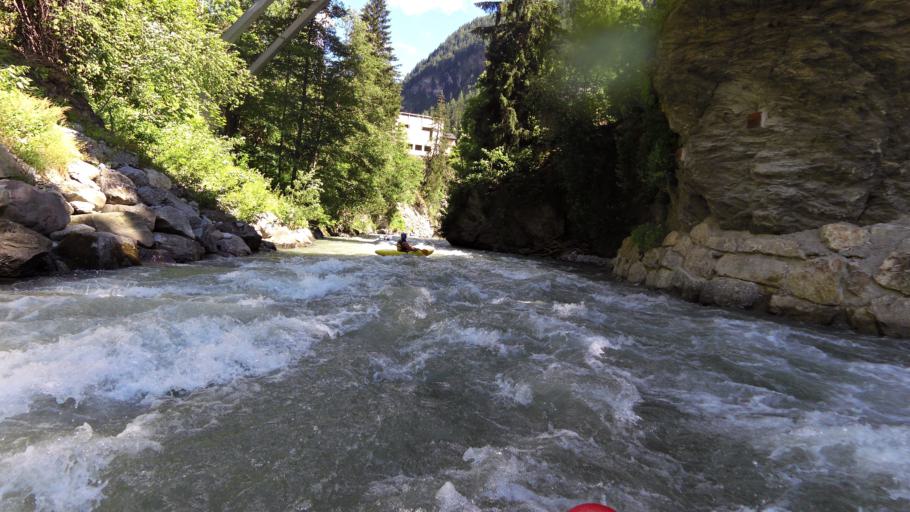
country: AT
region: Tyrol
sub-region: Politischer Bezirk Landeck
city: Strengen
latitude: 47.1258
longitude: 10.4612
